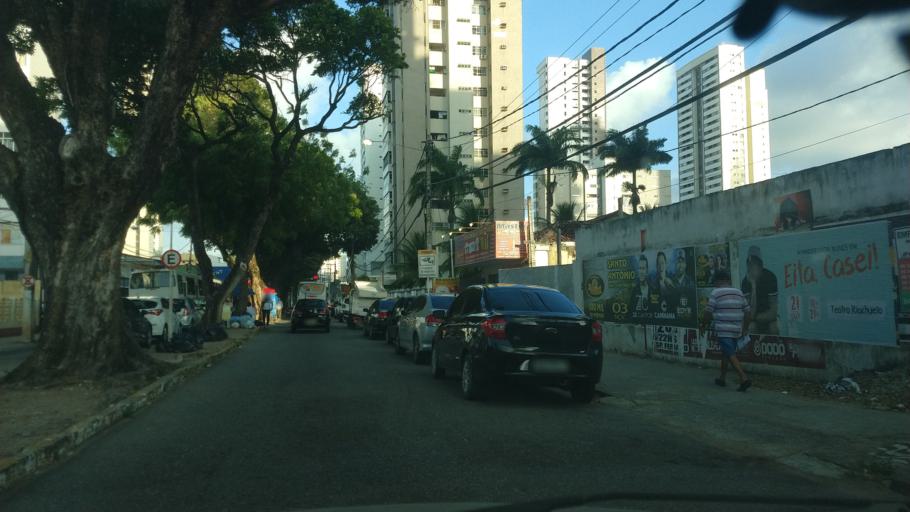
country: BR
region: Rio Grande do Norte
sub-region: Natal
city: Natal
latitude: -5.7869
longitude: -35.2023
